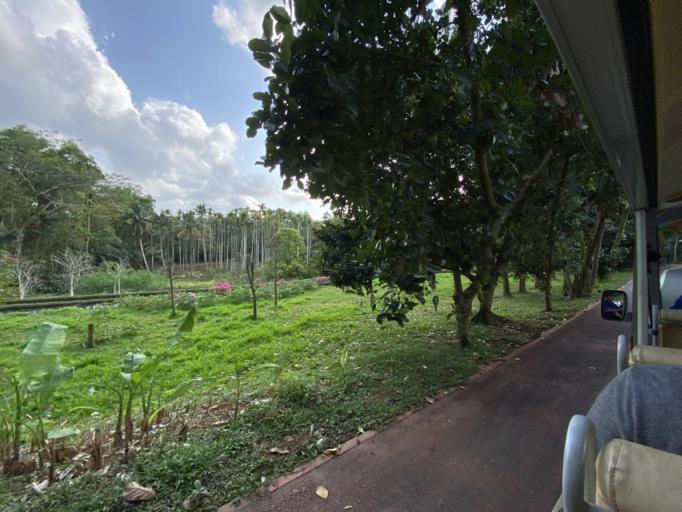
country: CN
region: Hainan
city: Nanqiao
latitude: 18.7317
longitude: 110.1908
